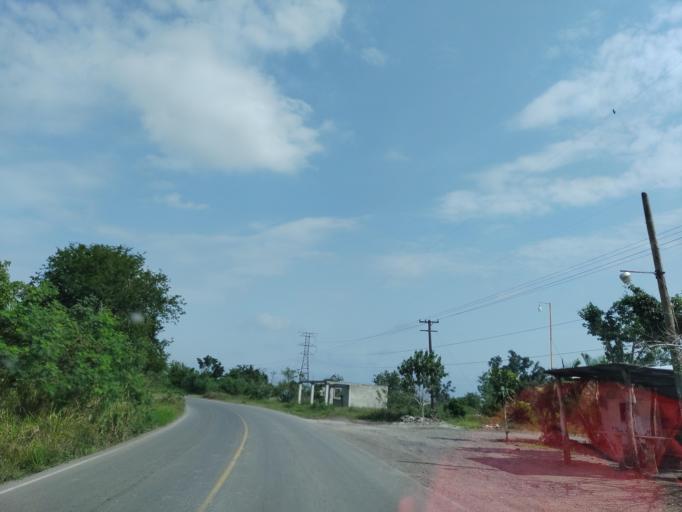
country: MX
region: Puebla
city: Espinal
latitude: 20.2764
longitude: -97.3308
